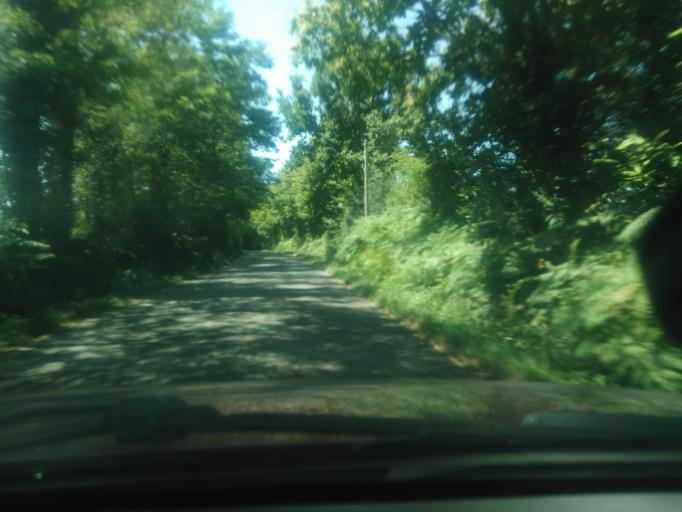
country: FR
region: Pays de la Loire
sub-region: Departement de la Vendee
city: Dompierre-sur-Yon
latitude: 46.7219
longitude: -1.3680
